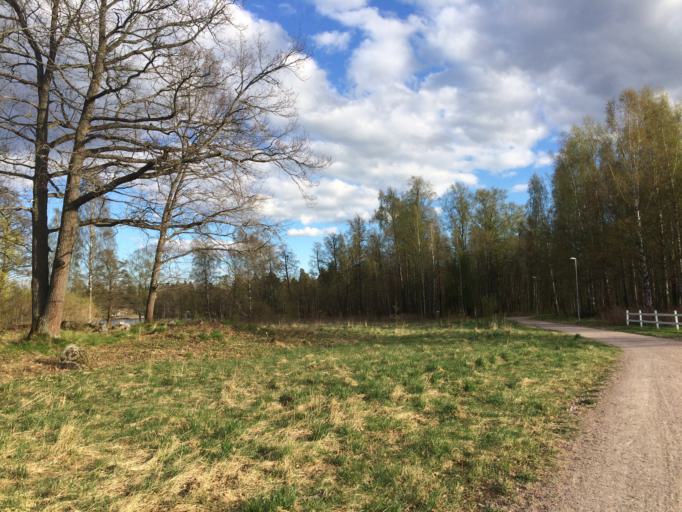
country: SE
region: Vaestmanland
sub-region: Hallstahammars Kommun
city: Hallstahammar
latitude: 59.6145
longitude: 16.2065
